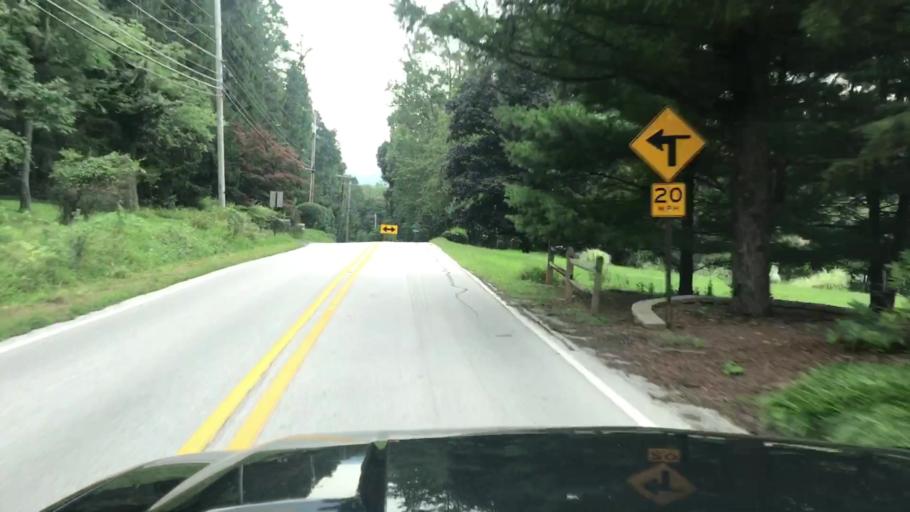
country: US
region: Pennsylvania
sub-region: Cumberland County
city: New Cumberland
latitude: 40.1847
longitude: -76.8726
